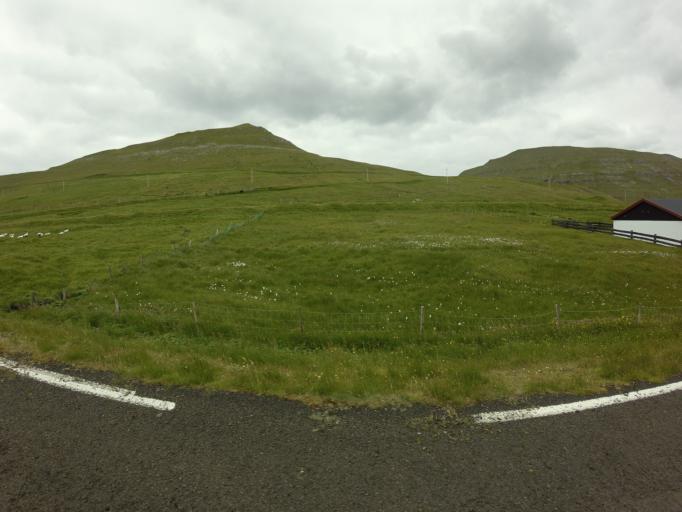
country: FO
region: Suduroy
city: Vagur
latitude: 61.4401
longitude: -6.7715
